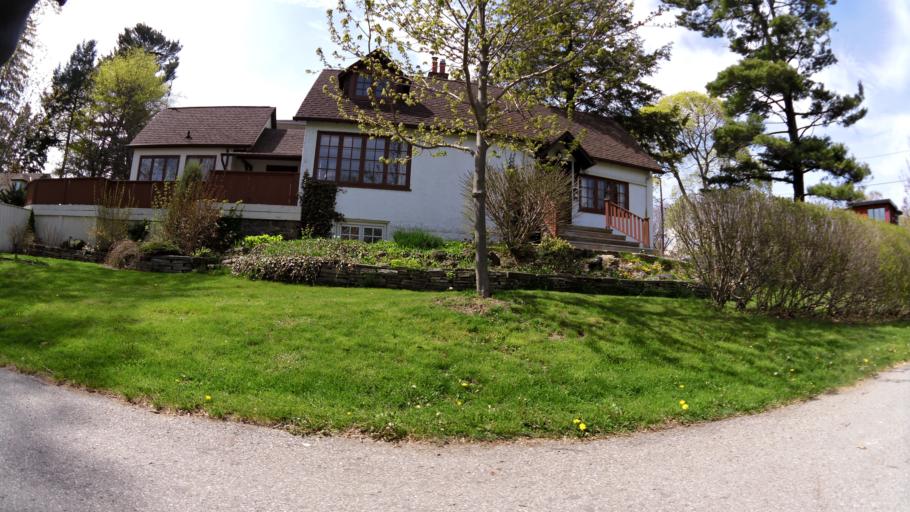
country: CA
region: Ontario
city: Mississauga
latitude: 43.5413
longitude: -79.5897
